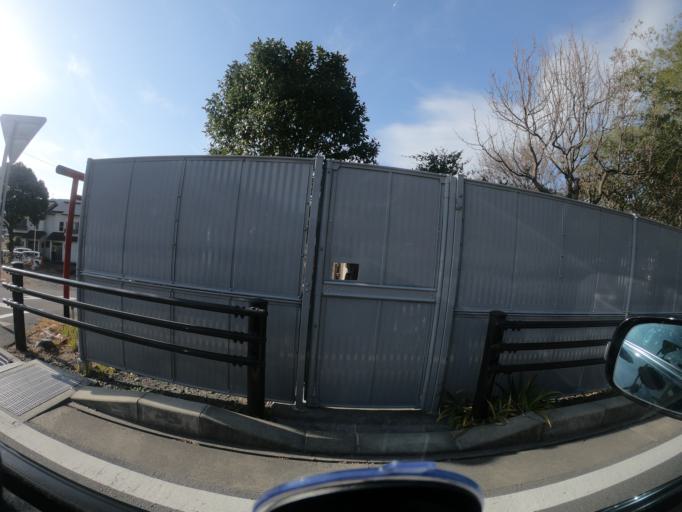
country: JP
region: Shizuoka
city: Kanaya
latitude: 35.0443
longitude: 138.0838
